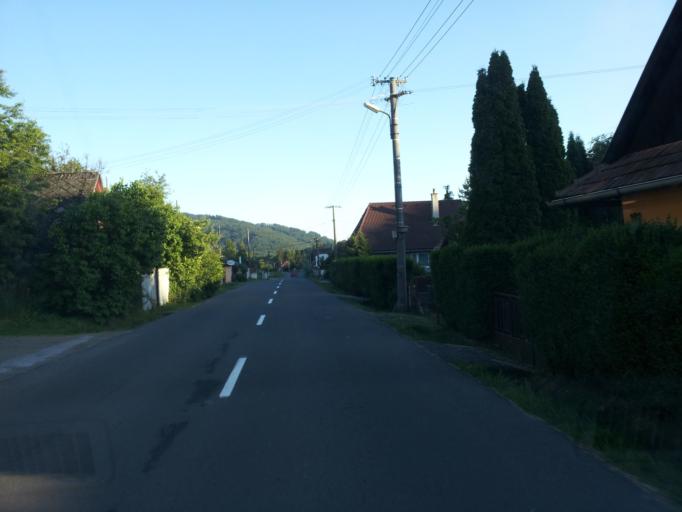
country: SK
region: Banskobystricky
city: Svaety Anton
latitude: 48.4158
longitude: 18.9394
